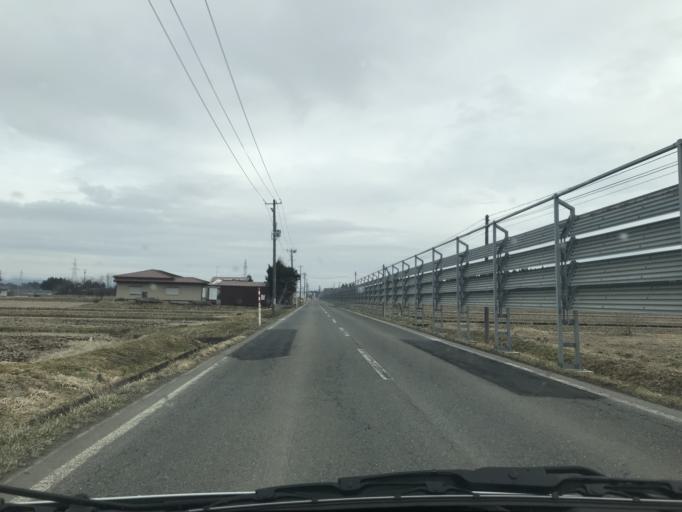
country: JP
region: Iwate
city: Kitakami
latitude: 39.3098
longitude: 141.0248
